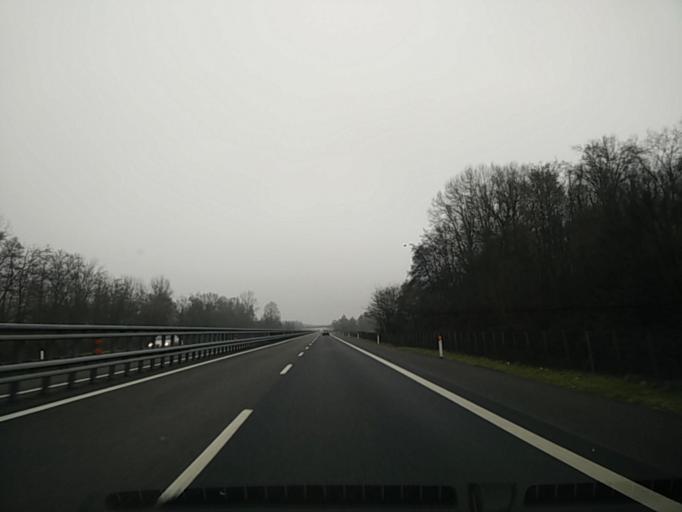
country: IT
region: Piedmont
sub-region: Provincia di Asti
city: Dusino
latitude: 44.9338
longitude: 7.9966
